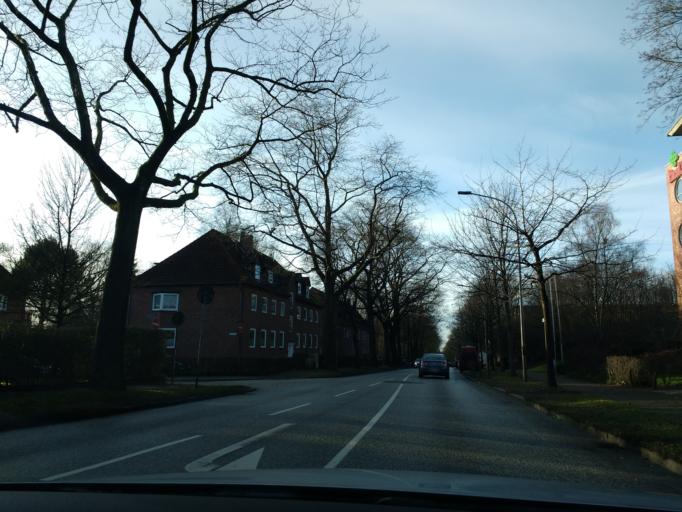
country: DE
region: Schleswig-Holstein
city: Itzehoe
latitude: 53.9313
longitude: 9.5255
